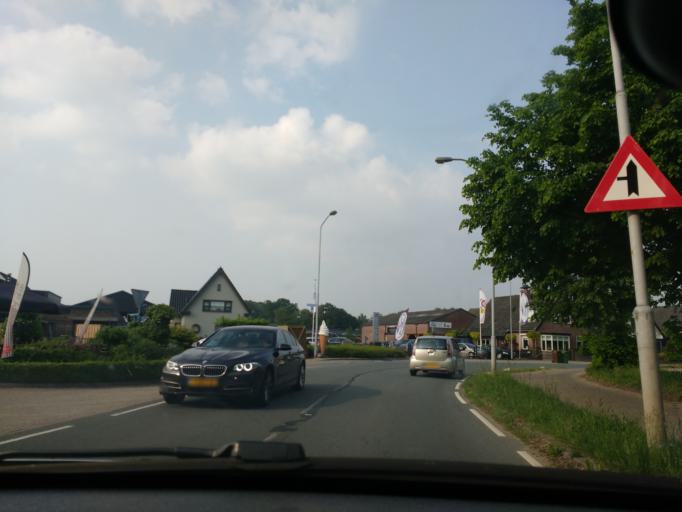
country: NL
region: Gelderland
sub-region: Gemeente Ede
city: Ederveen
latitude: 52.0337
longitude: 5.5978
